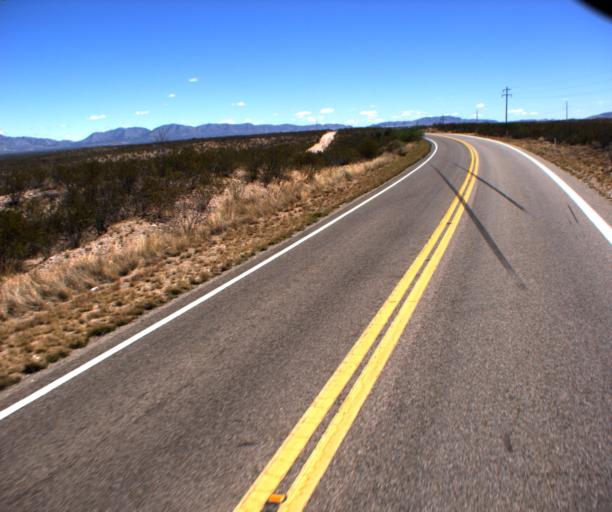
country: US
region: Arizona
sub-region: Cochise County
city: Tombstone
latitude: 31.7434
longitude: -110.1403
